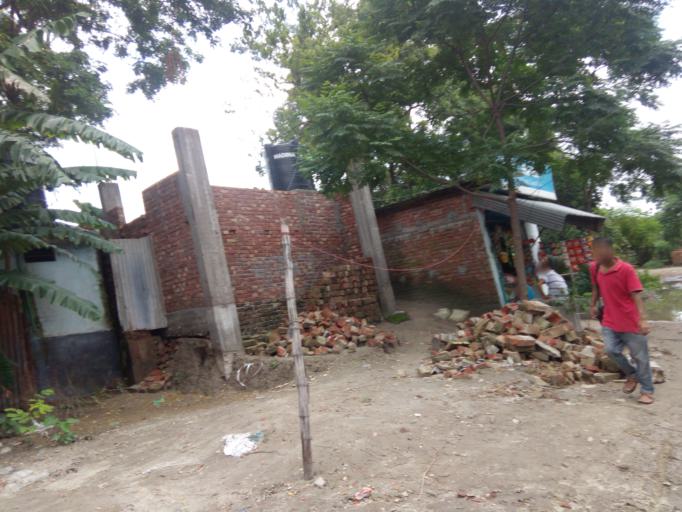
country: BD
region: Dhaka
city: Azimpur
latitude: 23.7347
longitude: 90.3496
